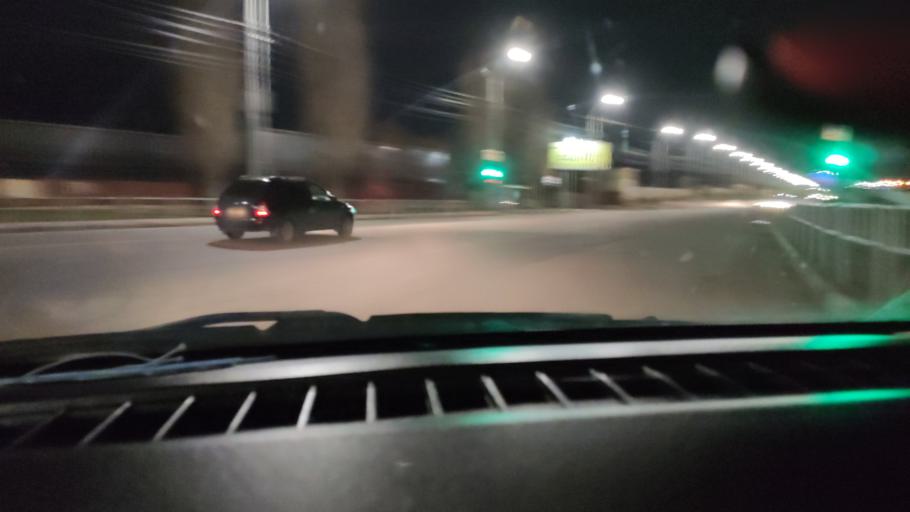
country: RU
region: Saratov
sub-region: Saratovskiy Rayon
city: Saratov
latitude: 51.5578
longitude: 46.0648
